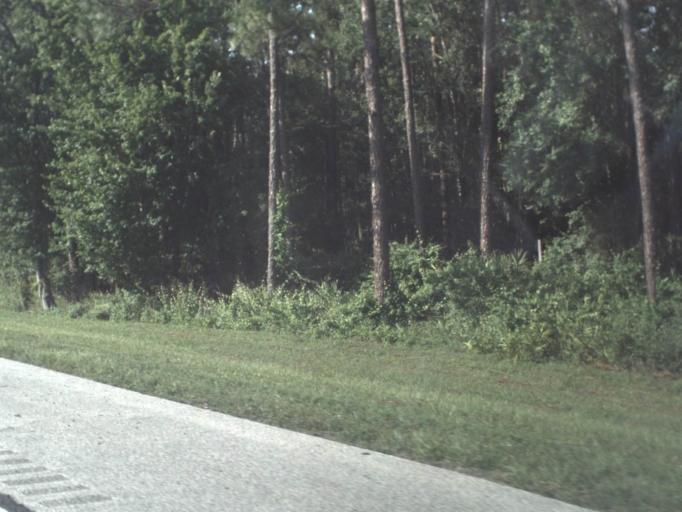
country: US
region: Florida
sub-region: Saint Johns County
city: Saint Augustine Shores
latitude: 29.7956
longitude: -81.3655
